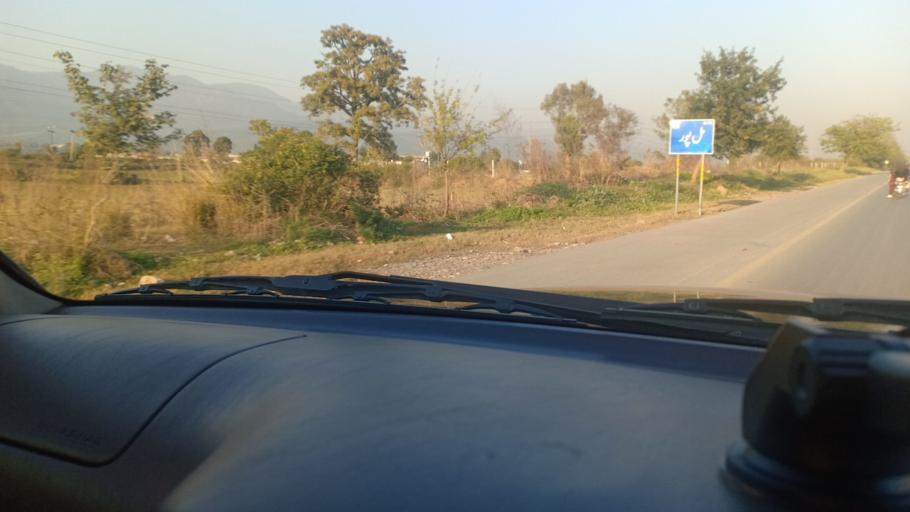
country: PK
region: Islamabad
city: Islamabad
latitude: 33.7272
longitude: 73.1409
